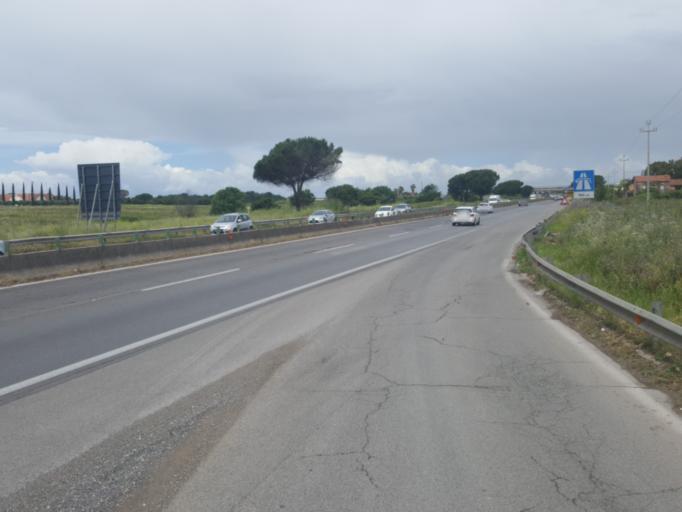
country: IT
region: Latium
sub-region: Provincia di Latina
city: Aprilia
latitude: 41.5697
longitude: 12.6682
